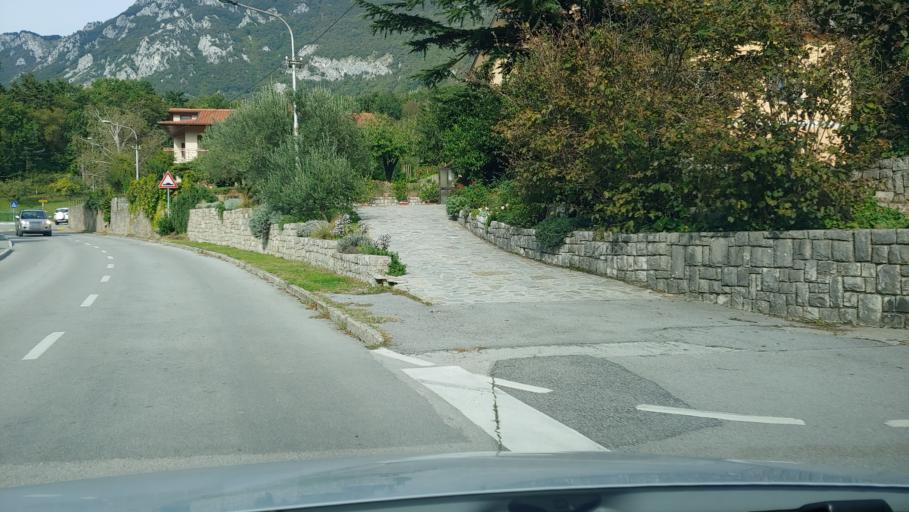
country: SI
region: Ajdovscina
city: Ajdovscina
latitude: 45.8926
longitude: 13.9067
